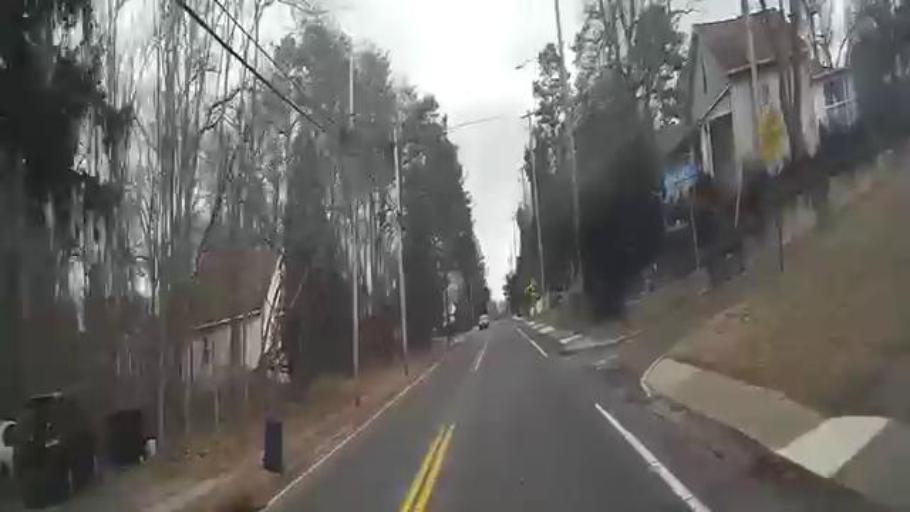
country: US
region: New Jersey
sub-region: Camden County
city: Clementon
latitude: 39.8012
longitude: -74.9734
